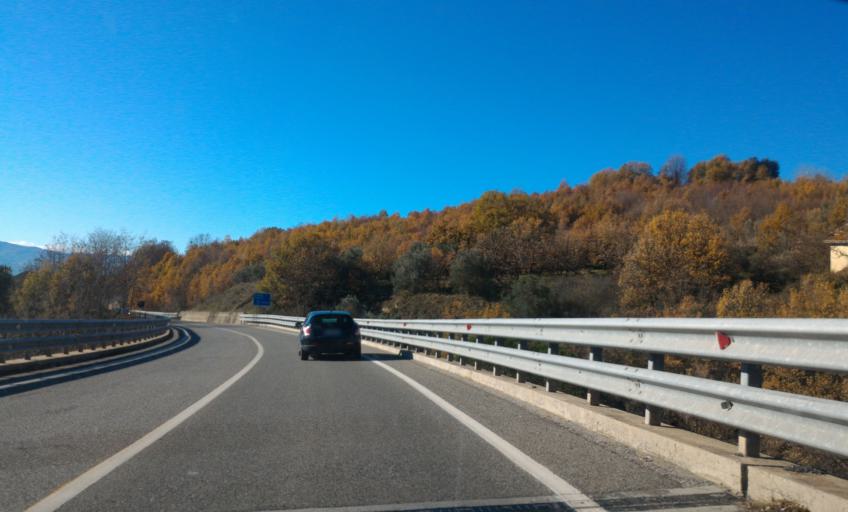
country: IT
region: Calabria
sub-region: Provincia di Cosenza
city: Celico
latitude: 39.3135
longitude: 16.3302
